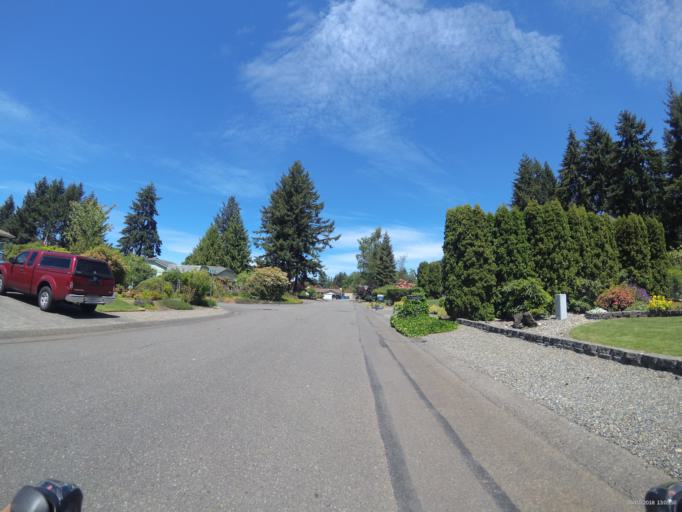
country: US
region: Washington
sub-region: Pierce County
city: University Place
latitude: 47.2031
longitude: -122.5666
